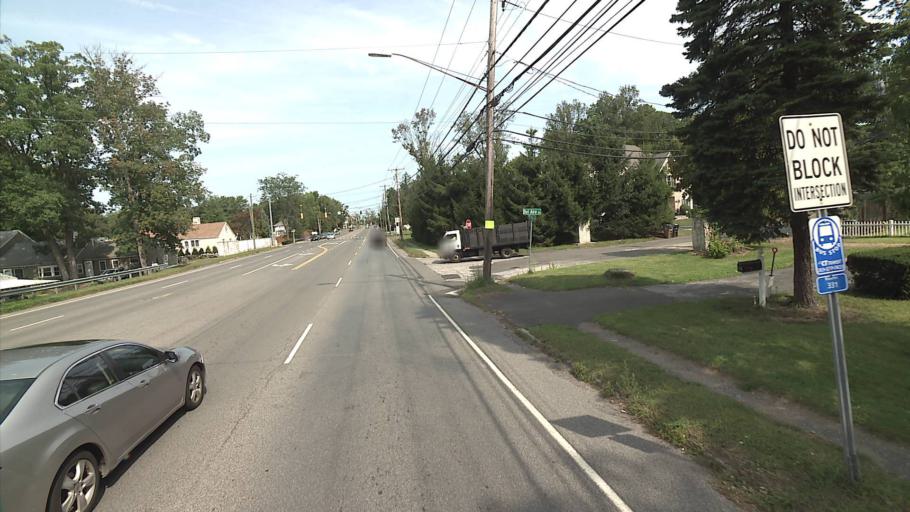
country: US
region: Connecticut
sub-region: Fairfield County
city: North Stamford
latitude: 41.0956
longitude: -73.5476
